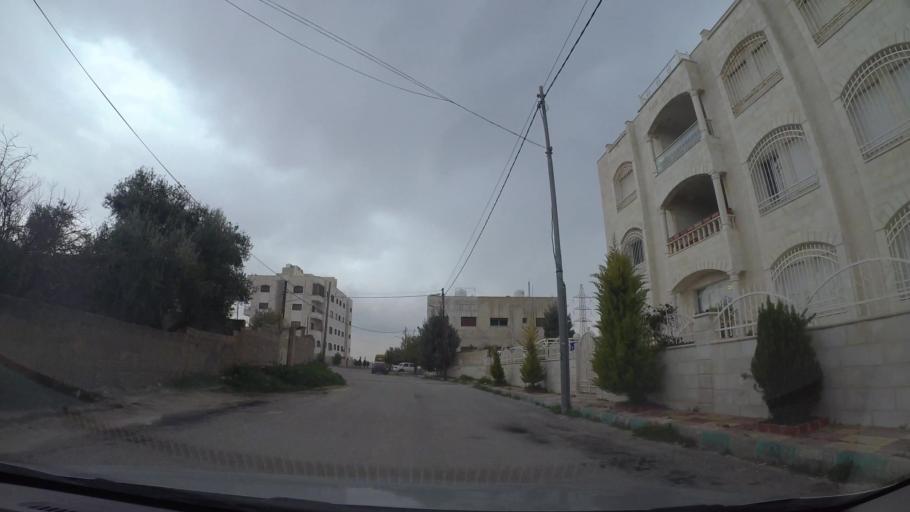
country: JO
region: Amman
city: Umm as Summaq
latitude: 31.9066
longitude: 35.8334
